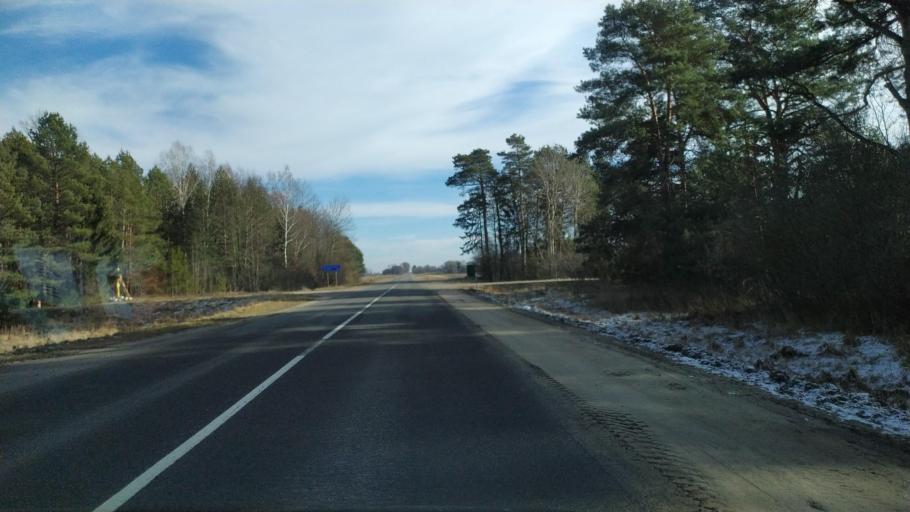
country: BY
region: Brest
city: Pruzhany
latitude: 52.5765
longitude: 24.3008
